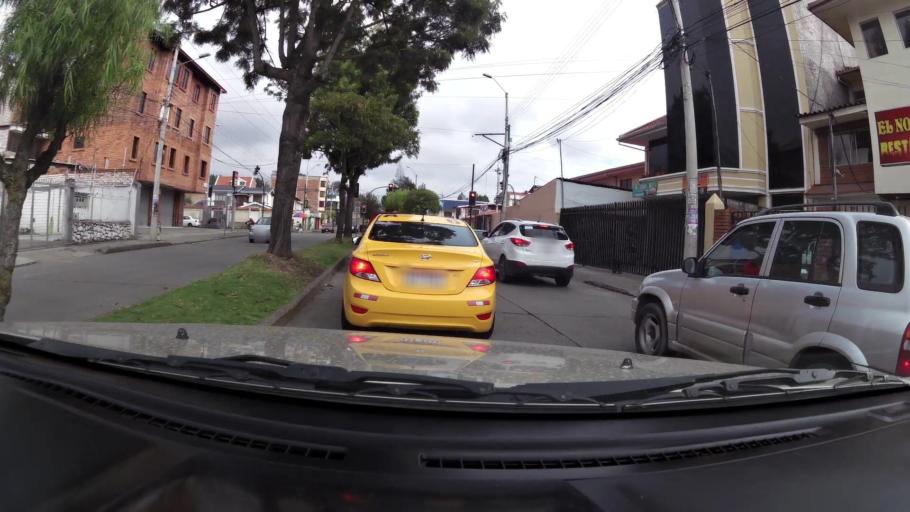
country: EC
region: Azuay
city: Cuenca
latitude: -2.8963
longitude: -78.9831
